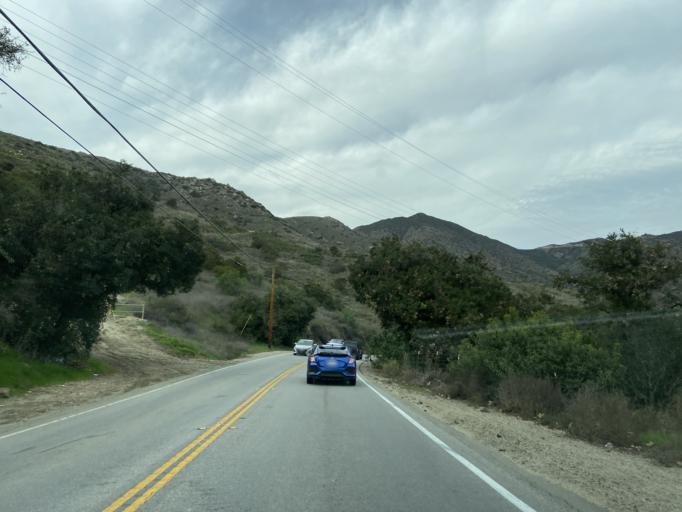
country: US
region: California
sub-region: San Diego County
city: Rainbow
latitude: 33.3524
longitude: -117.1126
